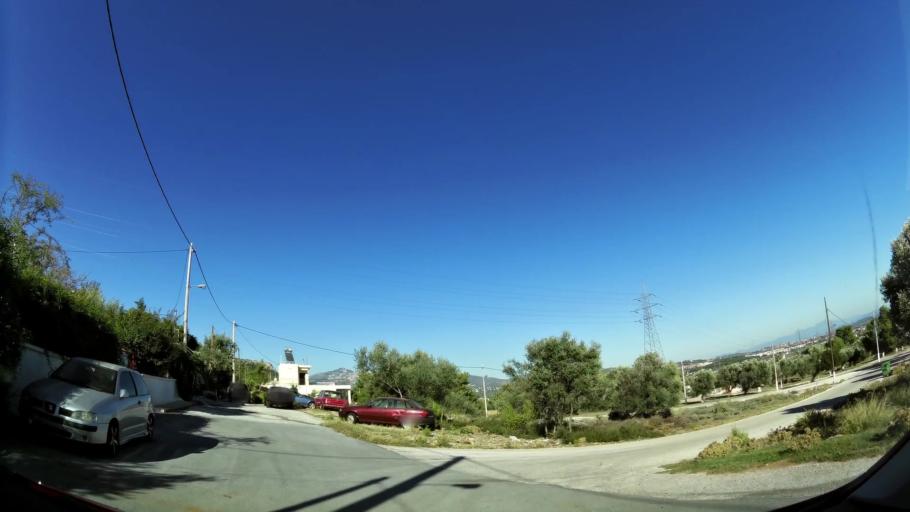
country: GR
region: Attica
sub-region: Nomarchia Anatolikis Attikis
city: Leondarion
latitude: 37.9929
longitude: 23.8420
